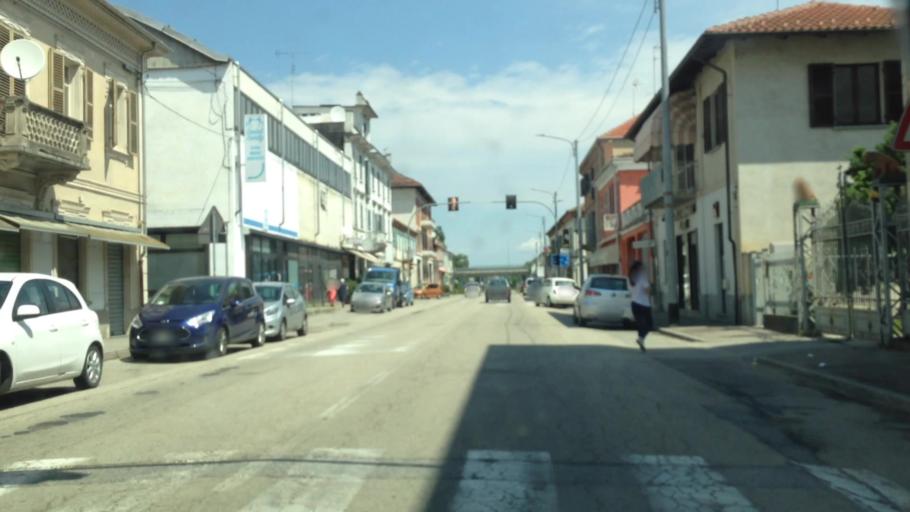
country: IT
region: Piedmont
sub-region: Provincia di Asti
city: Castell'Alfero
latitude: 44.9572
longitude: 8.2235
